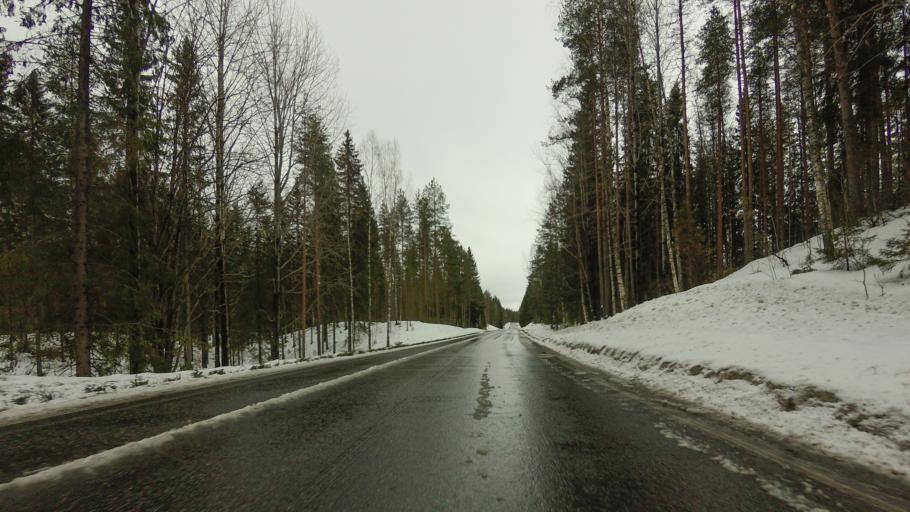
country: FI
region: Southern Savonia
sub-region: Savonlinna
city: Savonlinna
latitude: 61.9830
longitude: 28.8081
